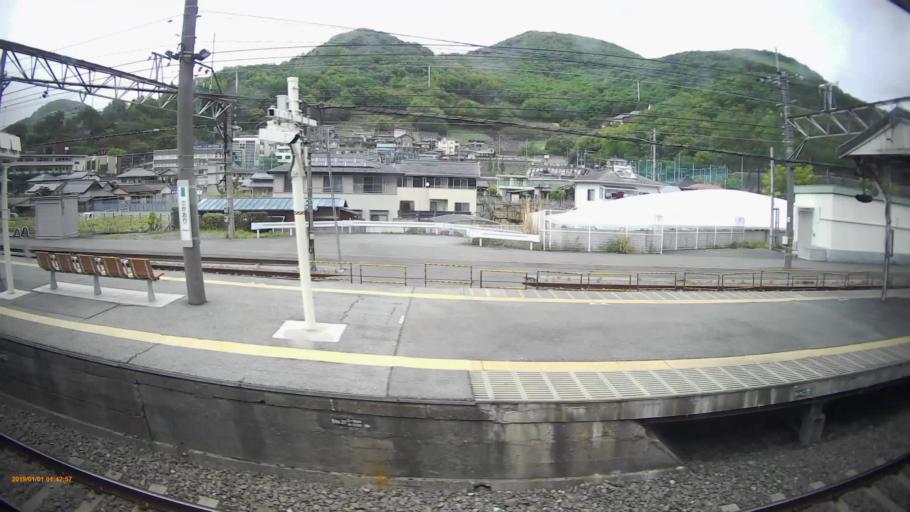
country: JP
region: Yamanashi
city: Kofu-shi
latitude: 35.6598
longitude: 138.5990
